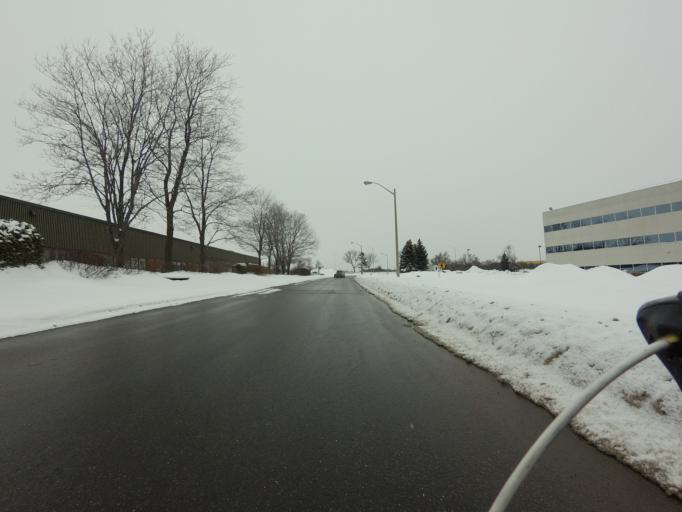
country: CA
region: Ontario
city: Bells Corners
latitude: 45.3466
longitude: -75.7927
